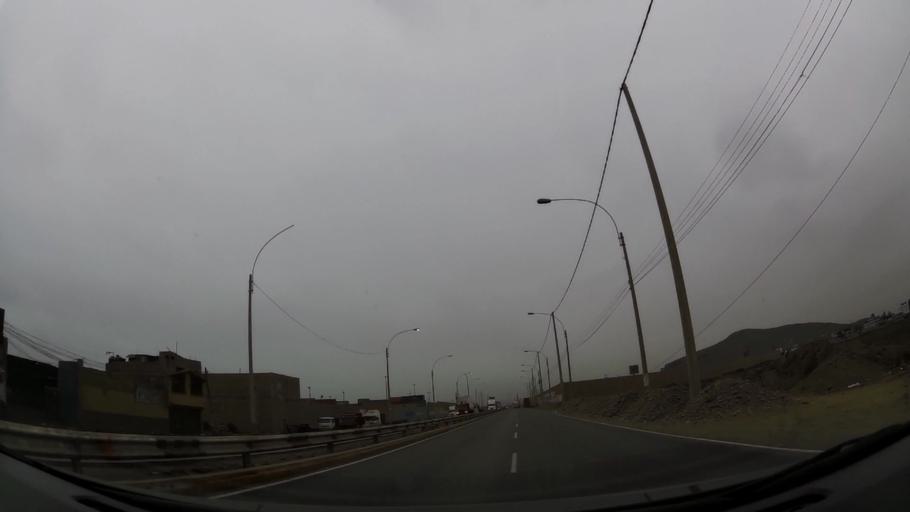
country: PE
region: Callao
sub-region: Callao
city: Callao
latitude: -12.0000
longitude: -77.1266
